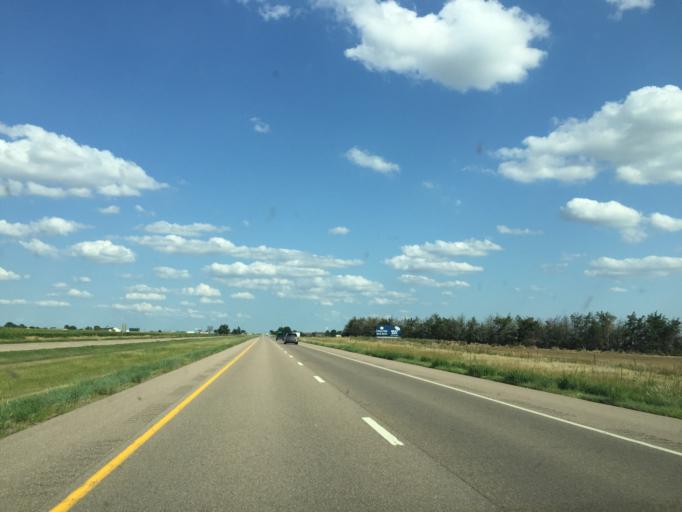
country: US
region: Kansas
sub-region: Gove County
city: Gove
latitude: 39.0633
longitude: -100.2532
